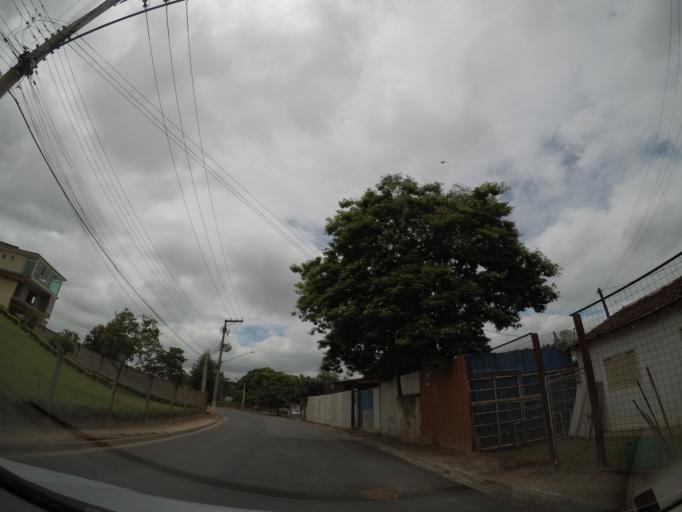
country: BR
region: Sao Paulo
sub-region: Louveira
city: Louveira
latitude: -23.0904
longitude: -46.9841
